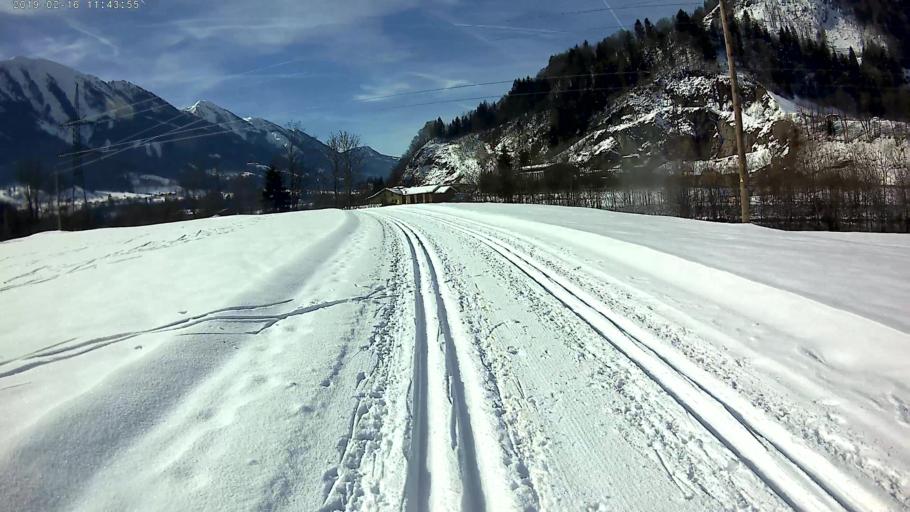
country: AT
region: Salzburg
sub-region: Politischer Bezirk Sankt Johann im Pongau
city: Sankt Johann im Pongau
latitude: 47.3314
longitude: 13.1911
